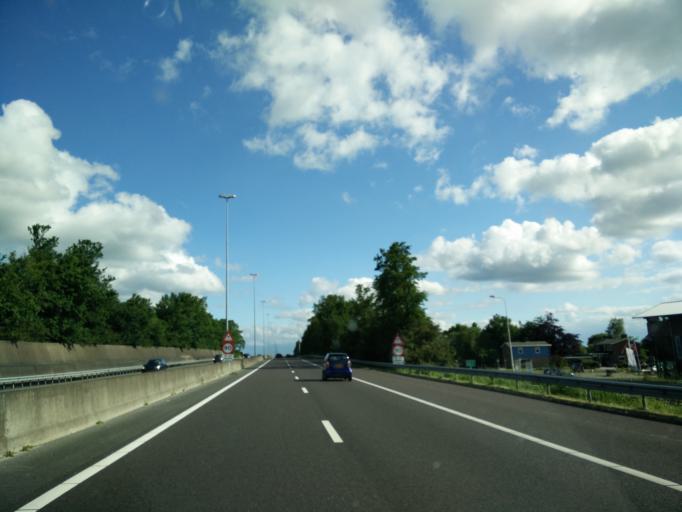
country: NL
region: Groningen
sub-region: Gemeente Haren
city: Haren
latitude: 53.1690
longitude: 6.5910
